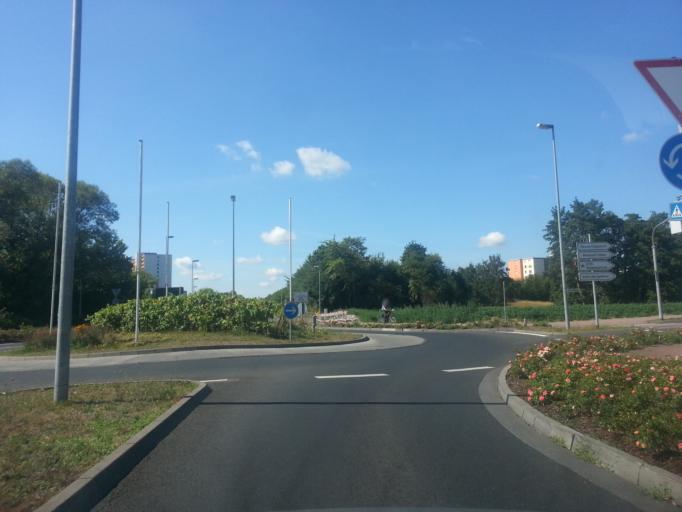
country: DE
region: Hesse
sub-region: Regierungsbezirk Darmstadt
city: Dietzenbach
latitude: 50.0198
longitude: 8.7816
